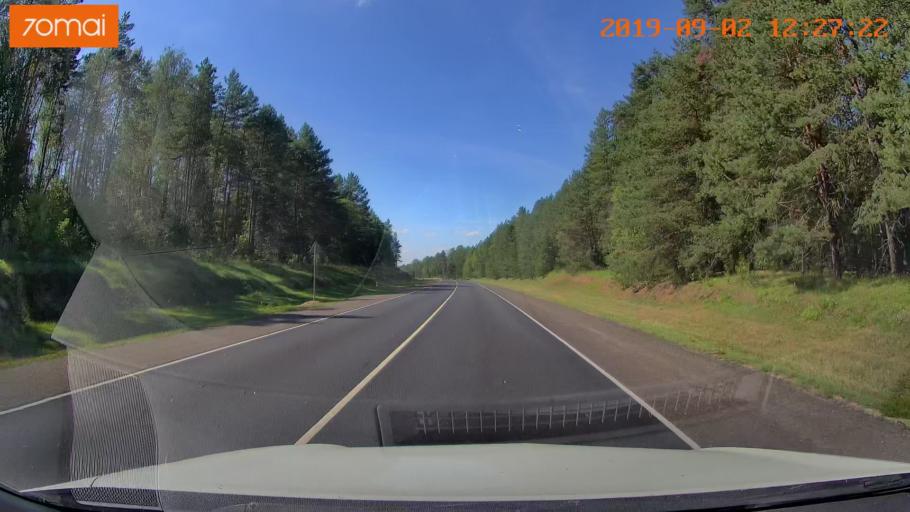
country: RU
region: Smolensk
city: Shumyachi
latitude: 53.8537
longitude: 32.5459
